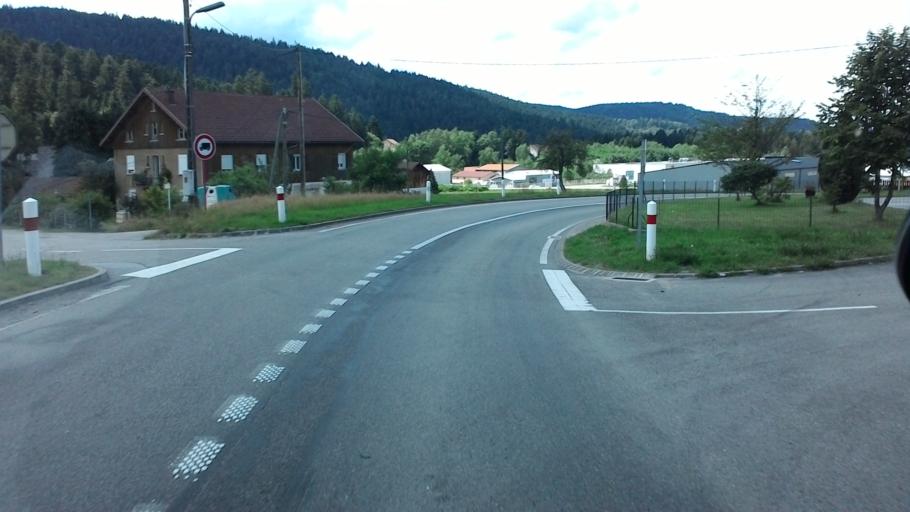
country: FR
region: Lorraine
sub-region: Departement des Vosges
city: Gerardmer
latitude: 48.0726
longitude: 6.8187
